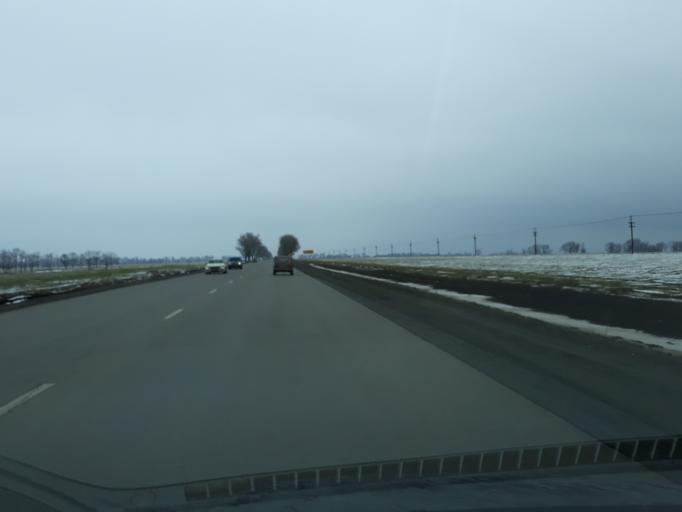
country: RU
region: Rostov
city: Primorka
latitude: 47.3085
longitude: 39.1301
